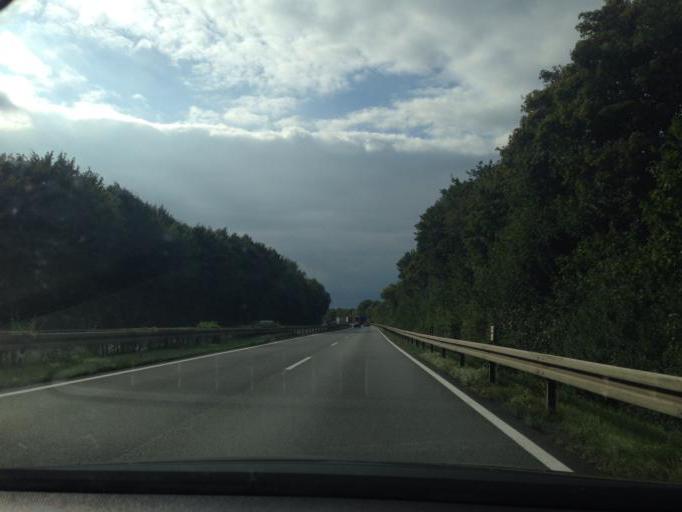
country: DE
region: Hesse
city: Allendorf an der Lahn
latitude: 50.5674
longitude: 8.5838
